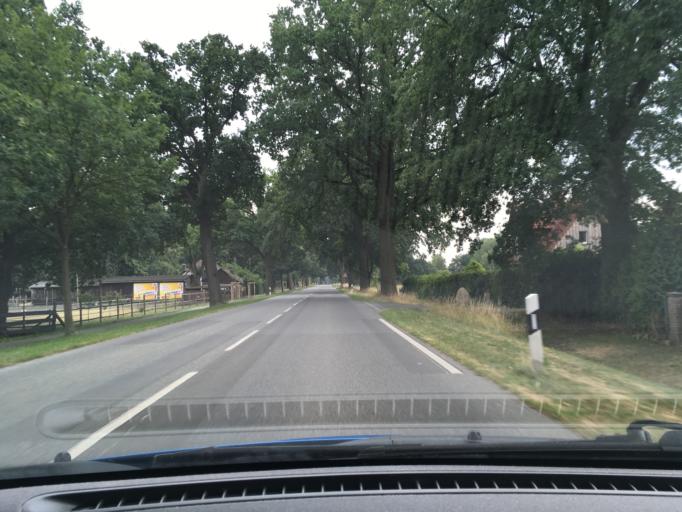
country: DE
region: Lower Saxony
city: Adelheidsdorf
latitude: 52.5446
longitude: 10.0533
